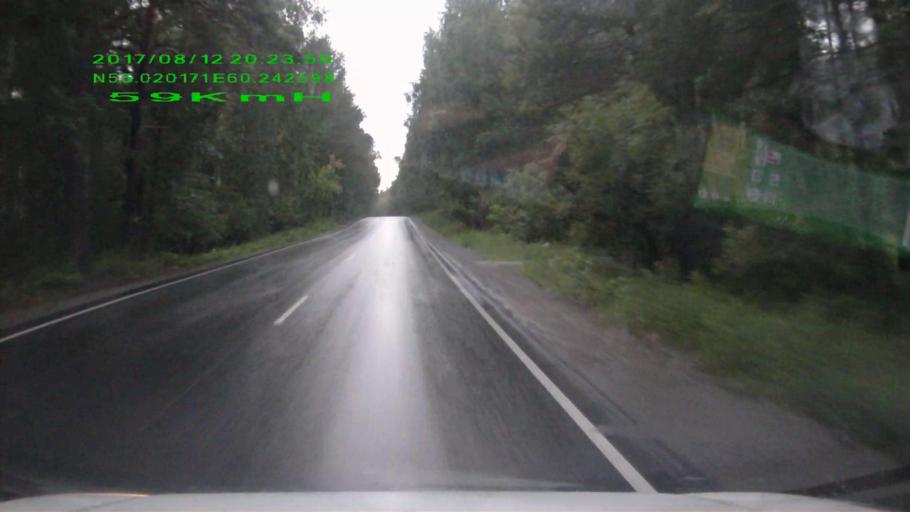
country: RU
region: Chelyabinsk
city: Chebarkul'
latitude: 55.0202
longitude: 60.2421
